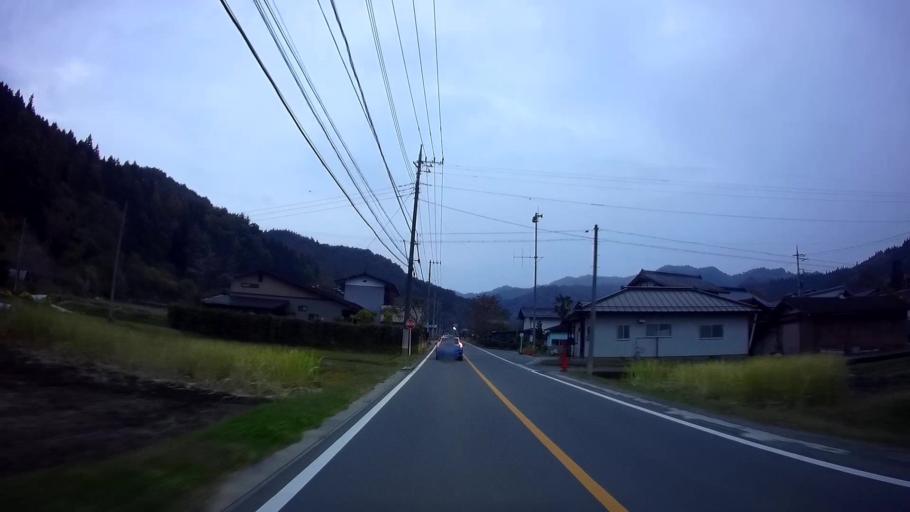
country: JP
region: Gunma
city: Nakanojomachi
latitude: 36.5360
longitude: 138.7857
